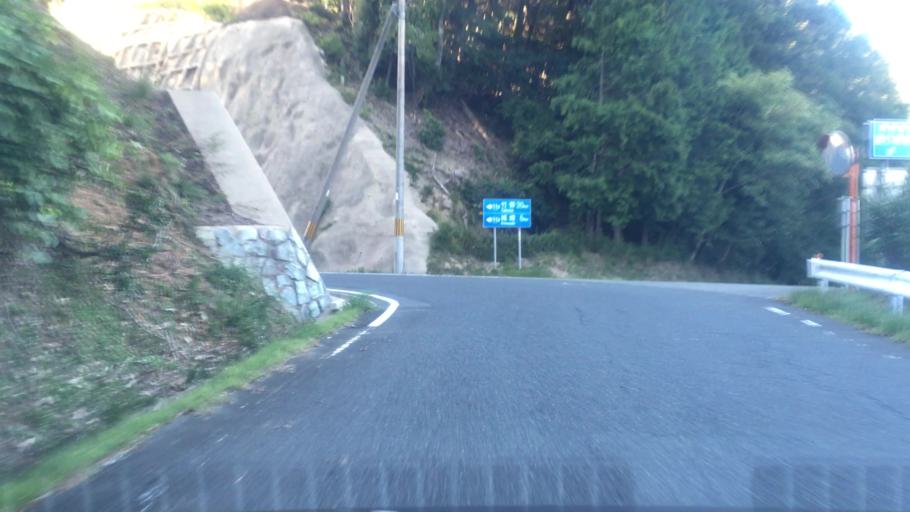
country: JP
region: Hyogo
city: Toyooka
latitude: 35.6186
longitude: 134.8730
